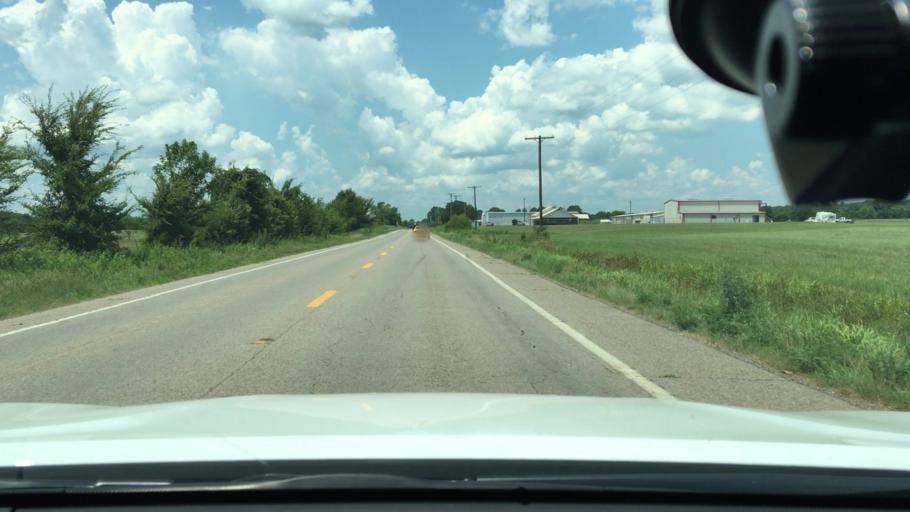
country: US
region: Arkansas
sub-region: Logan County
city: Booneville
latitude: 35.1477
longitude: -93.8622
